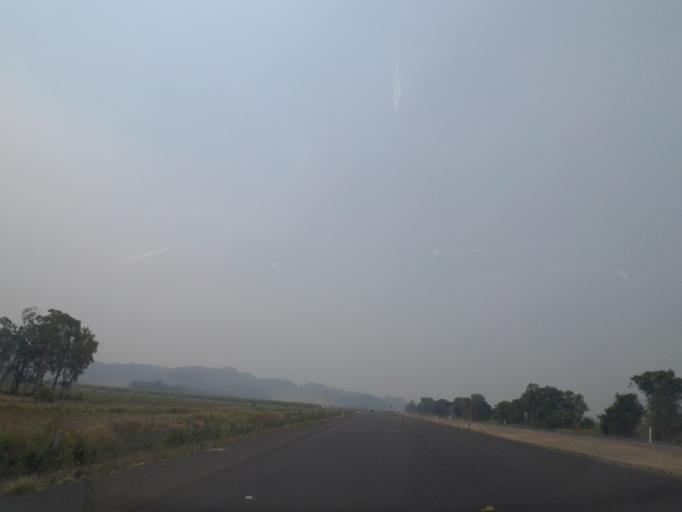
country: AU
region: New South Wales
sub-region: Ballina
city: Ballina
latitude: -28.8924
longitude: 153.4817
